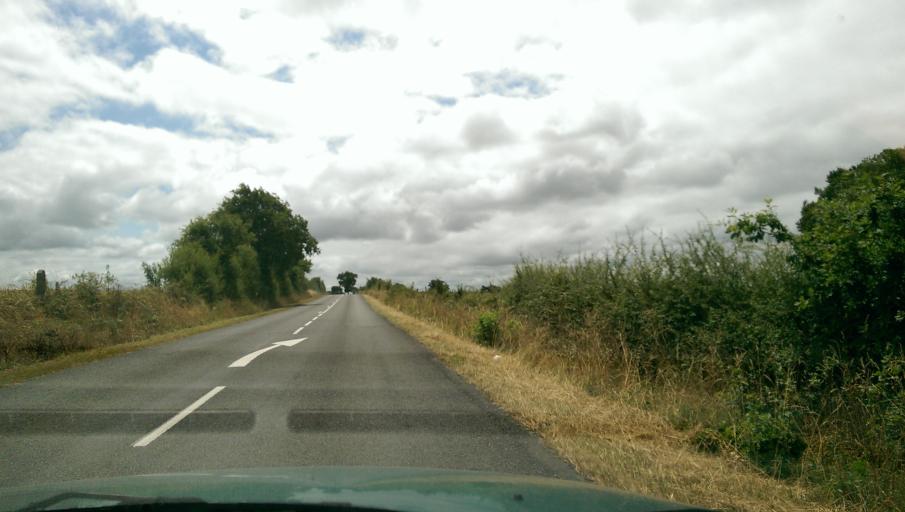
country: FR
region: Pays de la Loire
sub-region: Departement de la Loire-Atlantique
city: Aigrefeuille-sur-Maine
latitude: 47.0779
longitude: -1.3872
